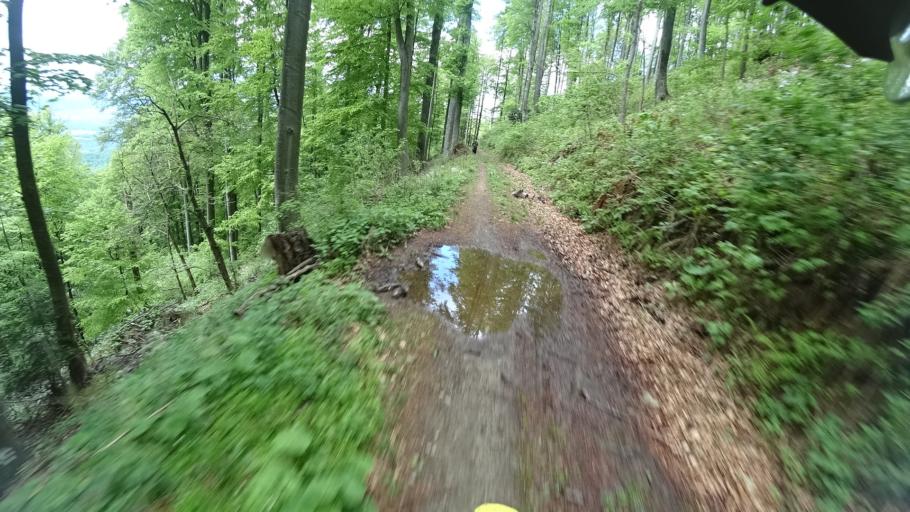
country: HR
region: Grad Zagreb
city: Kasina
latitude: 45.8927
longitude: 15.9315
